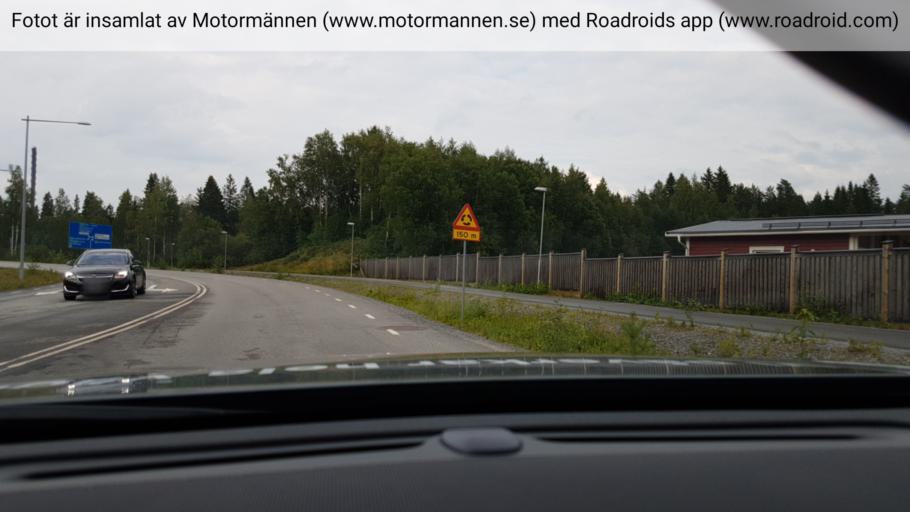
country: SE
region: Vaesterbotten
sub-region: Umea Kommun
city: Ersmark
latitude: 63.8454
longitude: 20.3424
